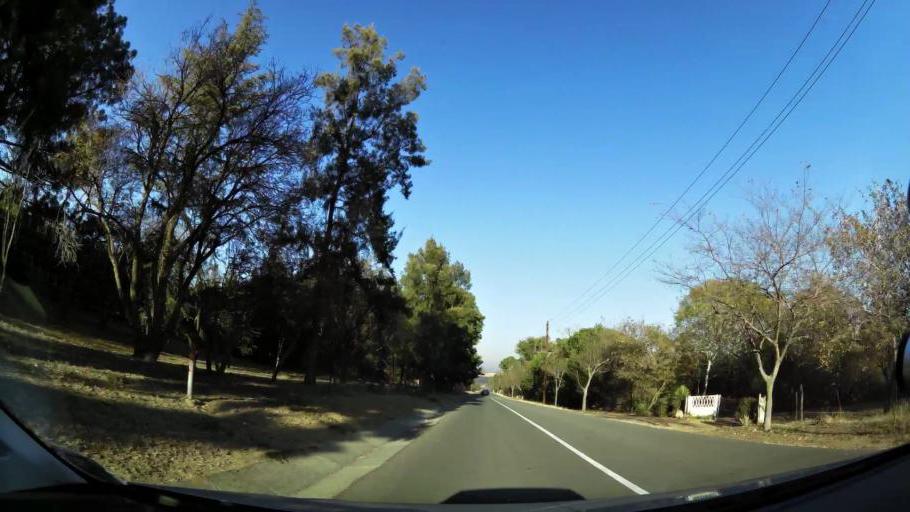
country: ZA
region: Gauteng
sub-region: City of Johannesburg Metropolitan Municipality
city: Midrand
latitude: -26.0237
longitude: 28.1407
